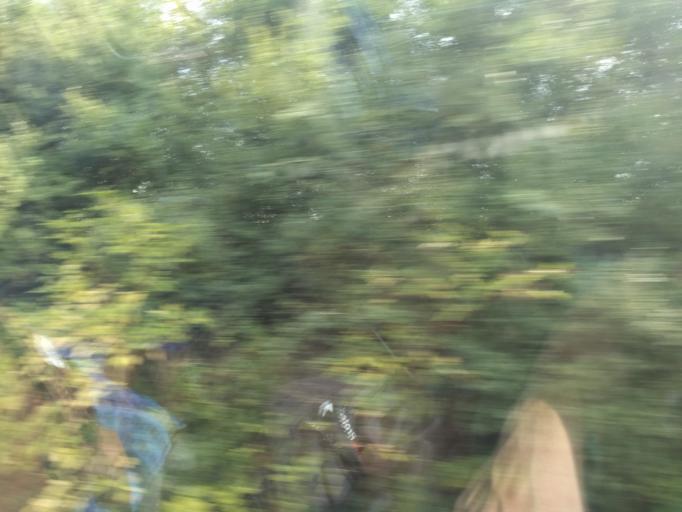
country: DE
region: Schleswig-Holstein
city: Heidekamp
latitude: 53.8385
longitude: 10.5129
